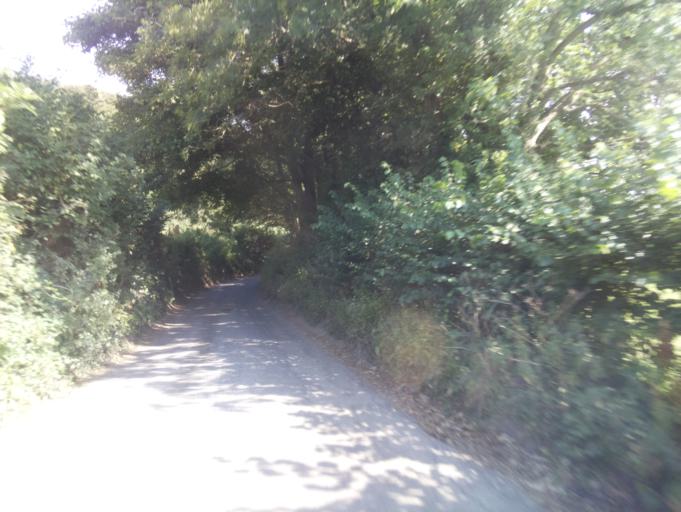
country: GB
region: England
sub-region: Gloucestershire
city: Dursley
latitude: 51.6840
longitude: -2.3185
